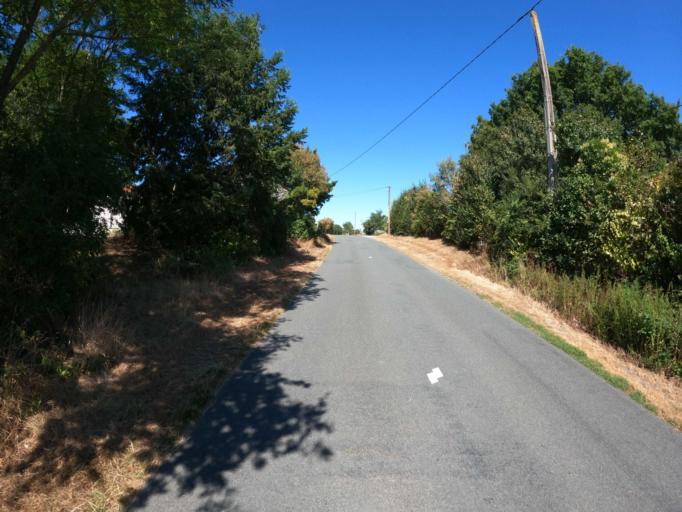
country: FR
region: Pays de la Loire
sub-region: Departement de la Vendee
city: Les Landes-Genusson
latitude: 46.9661
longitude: -1.1028
